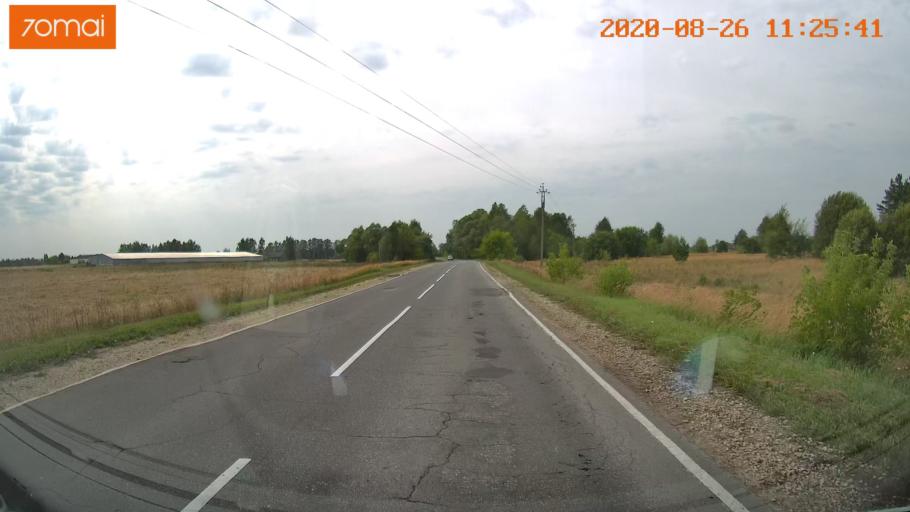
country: RU
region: Rjazan
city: Shilovo
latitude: 54.3399
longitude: 40.9599
